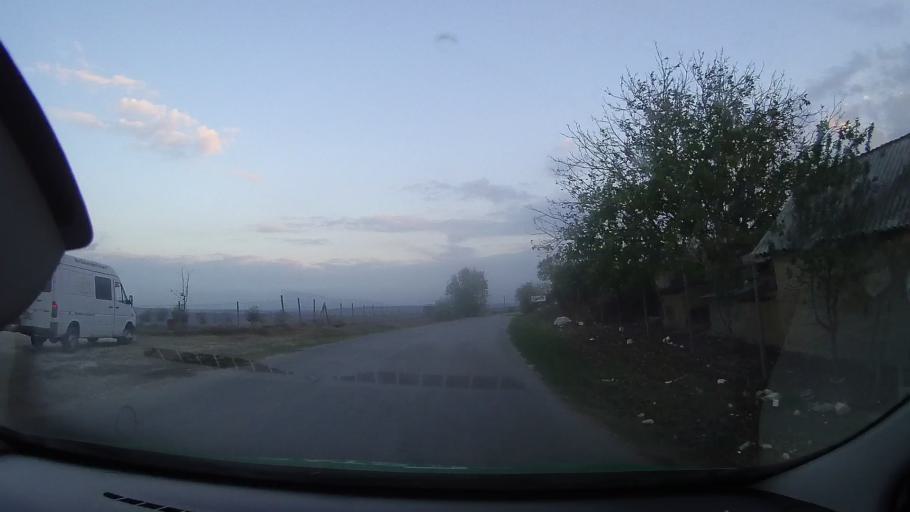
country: RO
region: Constanta
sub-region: Comuna Lipnita
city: Lipnita
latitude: 44.0966
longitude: 27.6107
